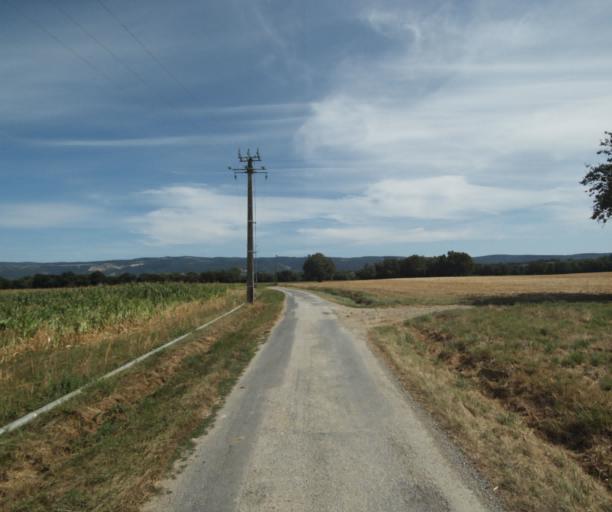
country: FR
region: Midi-Pyrenees
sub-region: Departement du Tarn
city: Soreze
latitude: 43.5063
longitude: 2.0620
